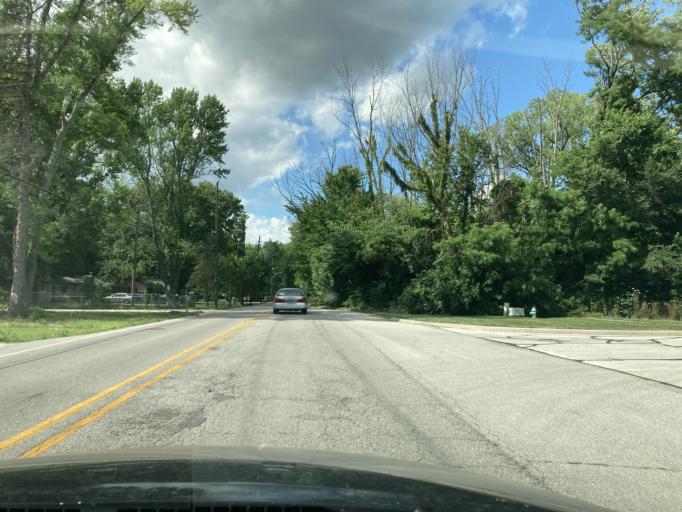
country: US
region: Indiana
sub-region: Marion County
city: Meridian Hills
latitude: 39.8586
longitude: -86.2120
